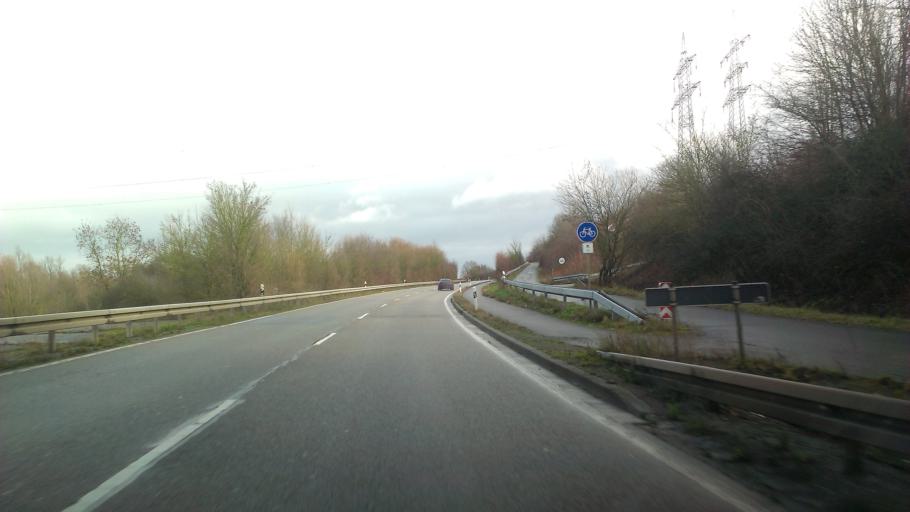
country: DE
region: Baden-Wuerttemberg
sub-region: Karlsruhe Region
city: Ubstadt-Weiher
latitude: 49.1495
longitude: 8.6178
